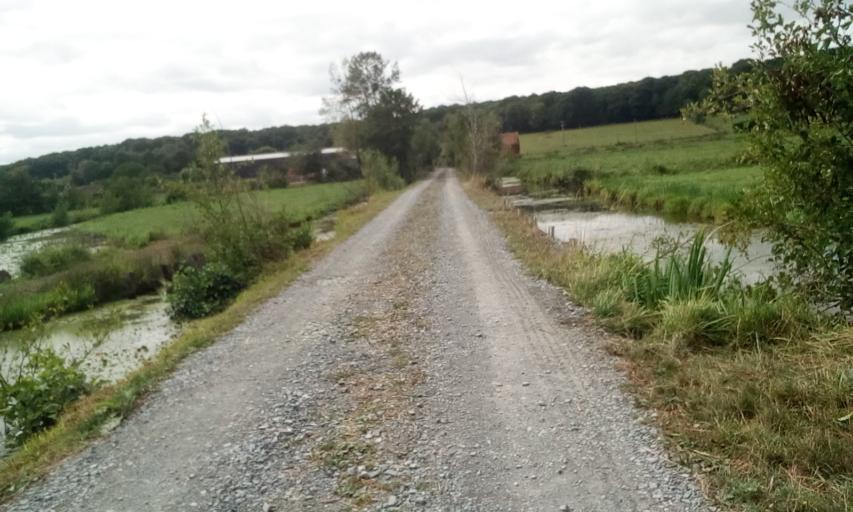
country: FR
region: Lower Normandy
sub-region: Departement du Calvados
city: Bavent
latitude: 49.2146
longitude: -0.1758
